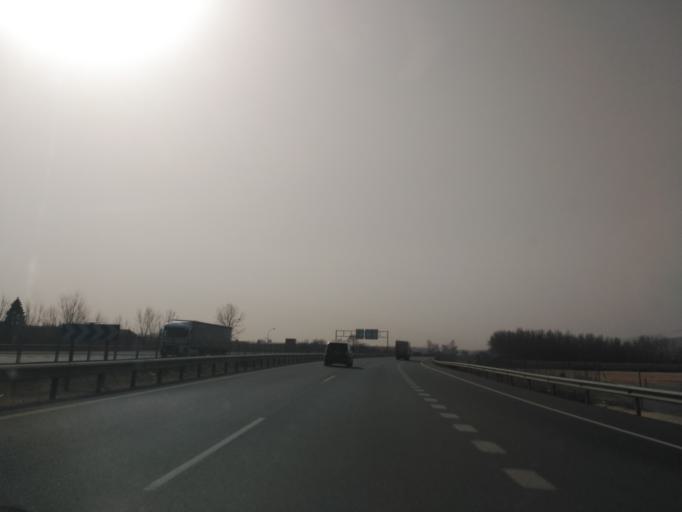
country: ES
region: Castille and Leon
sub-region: Provincia de Palencia
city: Venta de Banos
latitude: 41.9004
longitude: -4.5180
